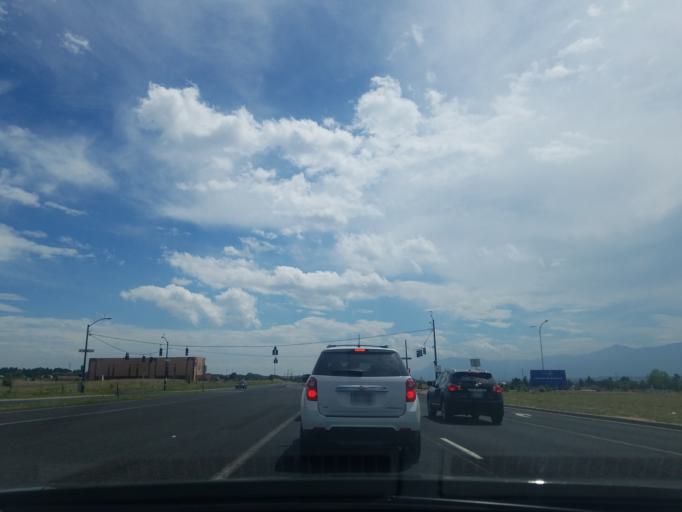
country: US
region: Colorado
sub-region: El Paso County
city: Air Force Academy
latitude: 38.9842
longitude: -104.7981
